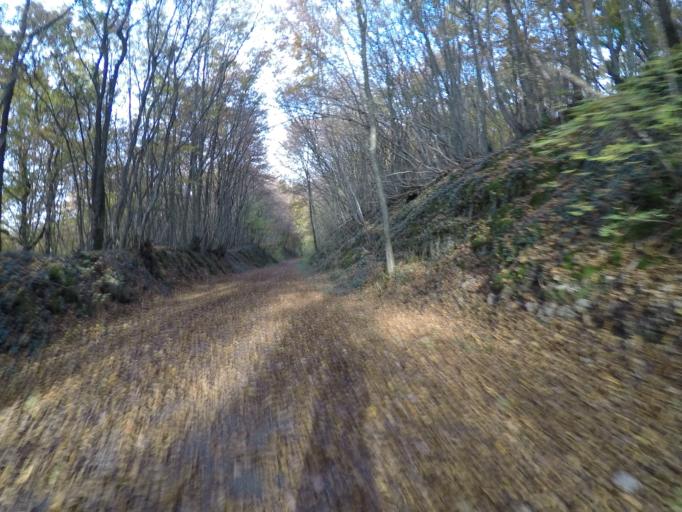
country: BE
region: Wallonia
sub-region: Province du Luxembourg
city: Hotton
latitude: 50.2813
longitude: 5.4826
